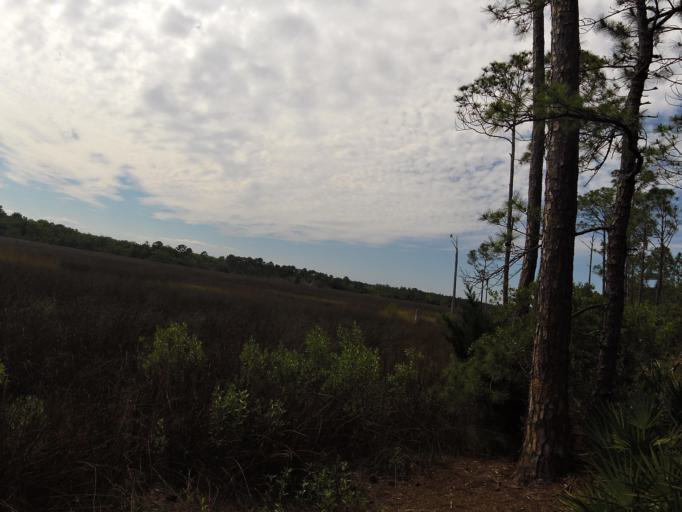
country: US
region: Florida
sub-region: Duval County
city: Atlantic Beach
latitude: 30.4544
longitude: -81.4759
